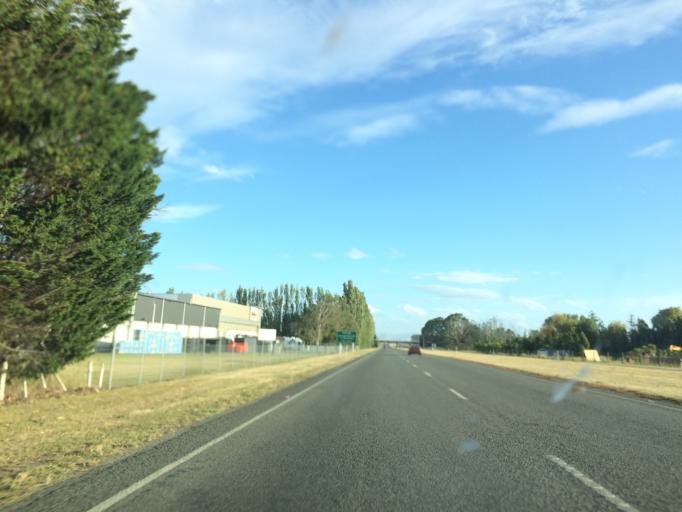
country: NZ
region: Canterbury
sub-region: Waimakariri District
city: Kaiapoi
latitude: -43.4024
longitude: 172.6431
